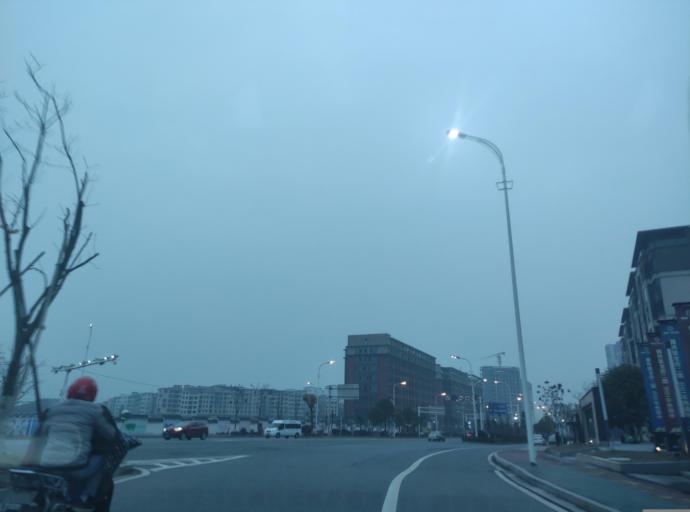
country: CN
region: Jiangxi Sheng
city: Pingxiang
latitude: 27.6684
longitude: 113.8497
